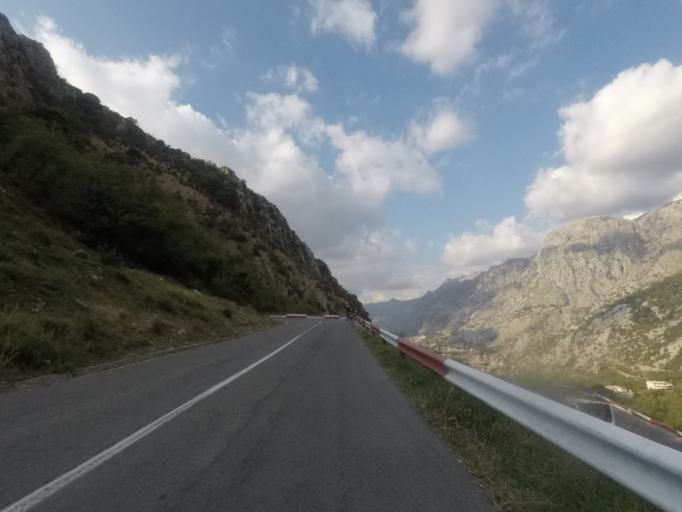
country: ME
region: Kotor
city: Kotor
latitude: 42.4059
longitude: 18.7646
